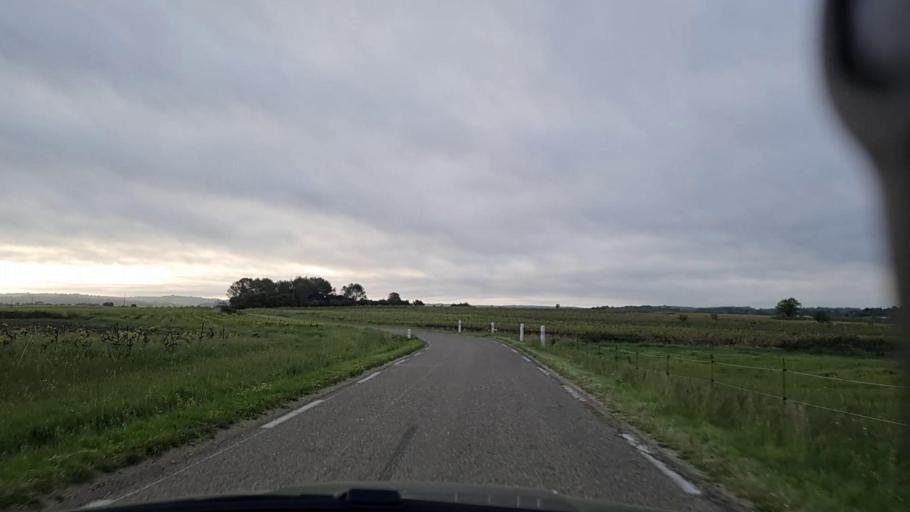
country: FR
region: Languedoc-Roussillon
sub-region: Departement du Gard
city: Villevieille
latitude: 43.8271
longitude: 4.1098
